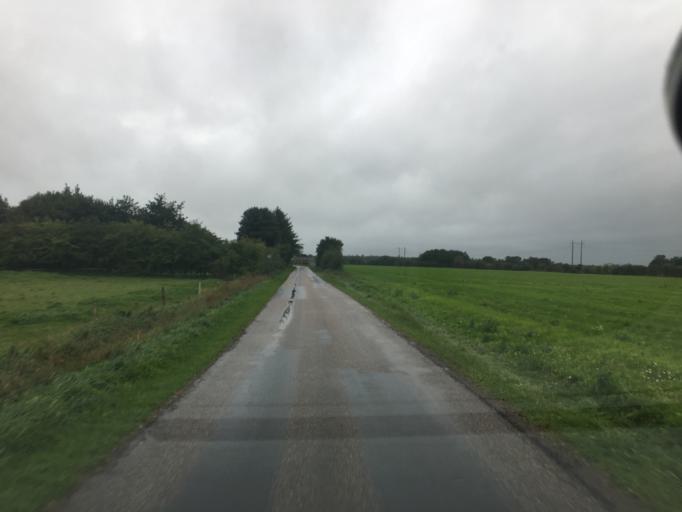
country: DE
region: Schleswig-Holstein
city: Bramstedtlund
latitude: 54.9577
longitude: 9.0456
